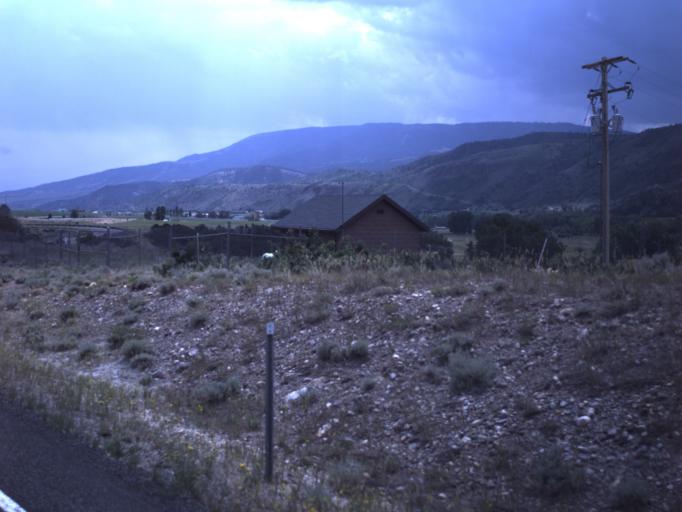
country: US
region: Utah
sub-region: Summit County
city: Francis
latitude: 40.4605
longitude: -110.8263
